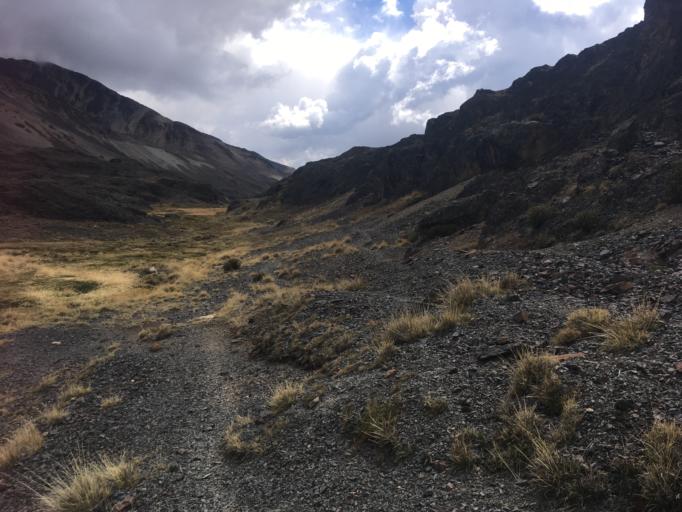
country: BO
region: La Paz
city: La Paz
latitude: -16.3942
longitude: -67.9707
